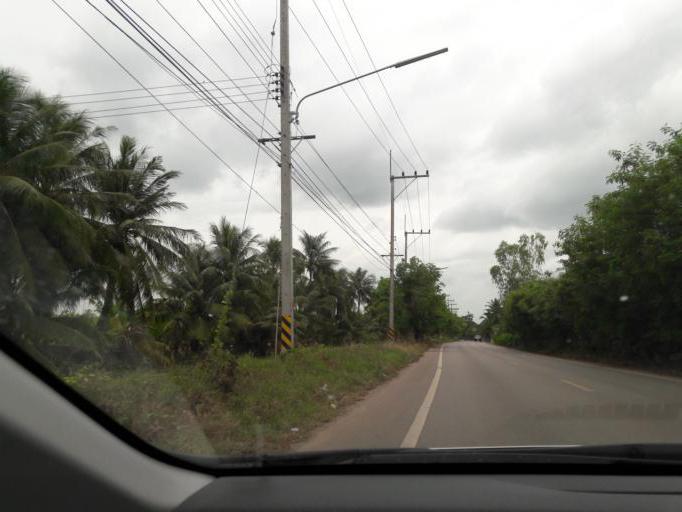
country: TH
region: Samut Sakhon
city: Ban Phaeo
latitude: 13.5653
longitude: 100.0436
